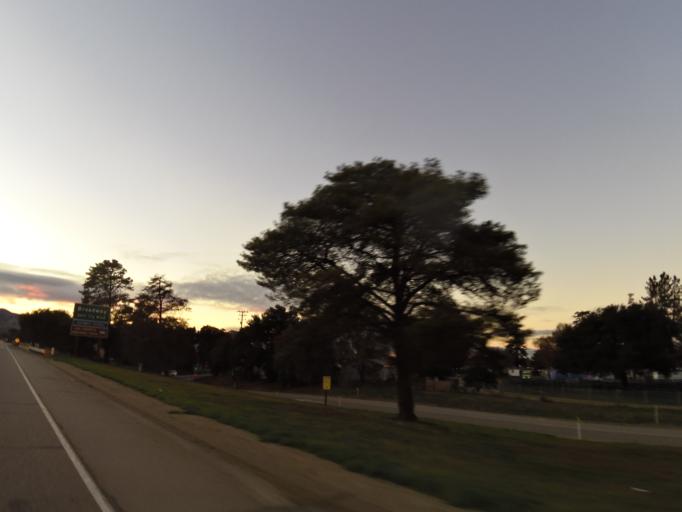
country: US
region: California
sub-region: Monterey County
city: King City
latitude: 36.2033
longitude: -121.1284
